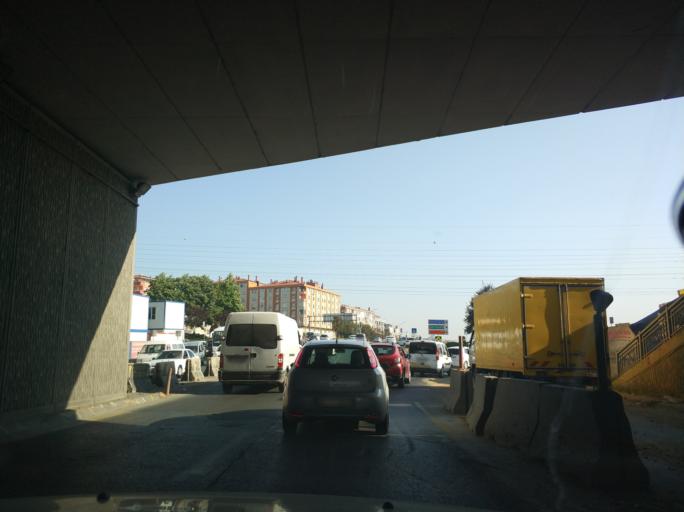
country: TR
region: Istanbul
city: Sultangazi
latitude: 41.0850
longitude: 28.9081
